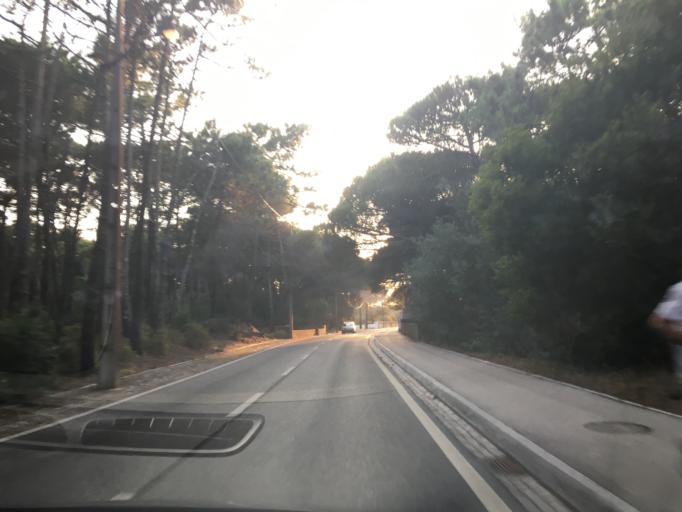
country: PT
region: Lisbon
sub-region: Sintra
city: Colares
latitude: 38.8308
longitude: -9.4460
